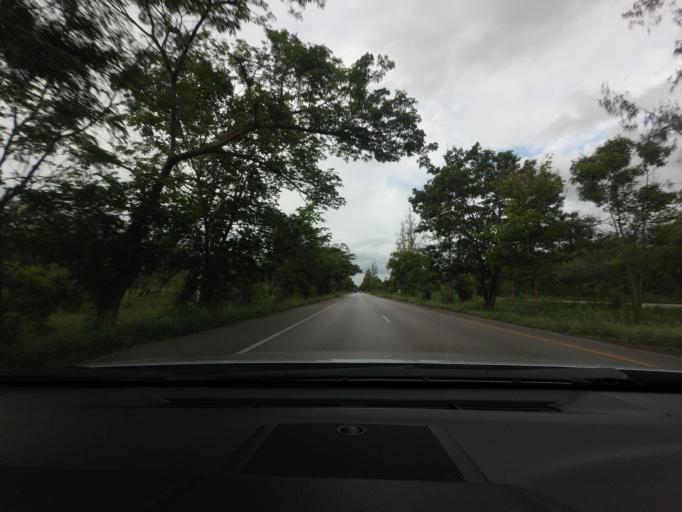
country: TH
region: Phetchaburi
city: Cha-am
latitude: 12.6933
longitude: 99.9024
